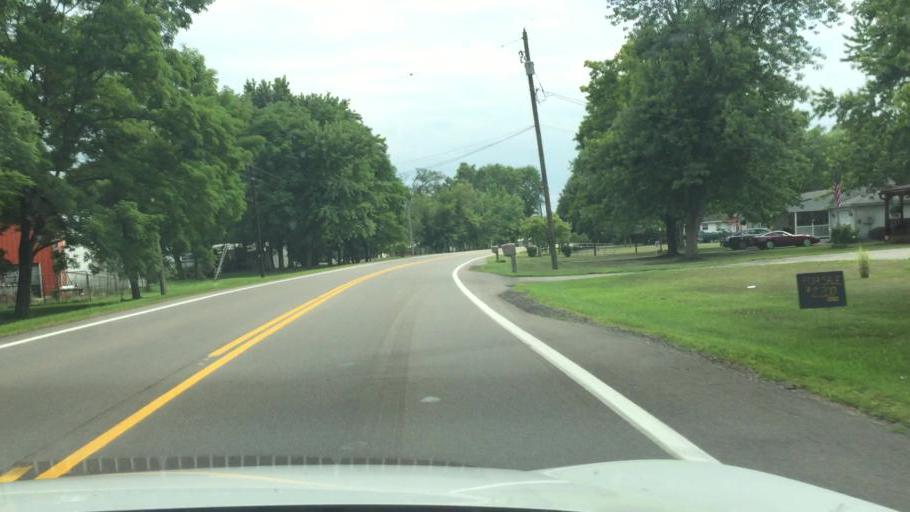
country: US
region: Ohio
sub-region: Champaign County
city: Mechanicsburg
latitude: 40.0242
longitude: -83.6588
